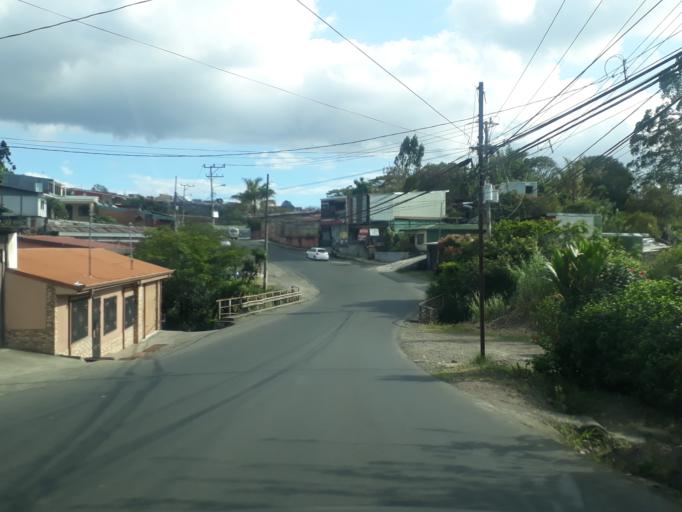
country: CR
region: San Jose
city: Purral
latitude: 9.9777
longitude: -84.0321
